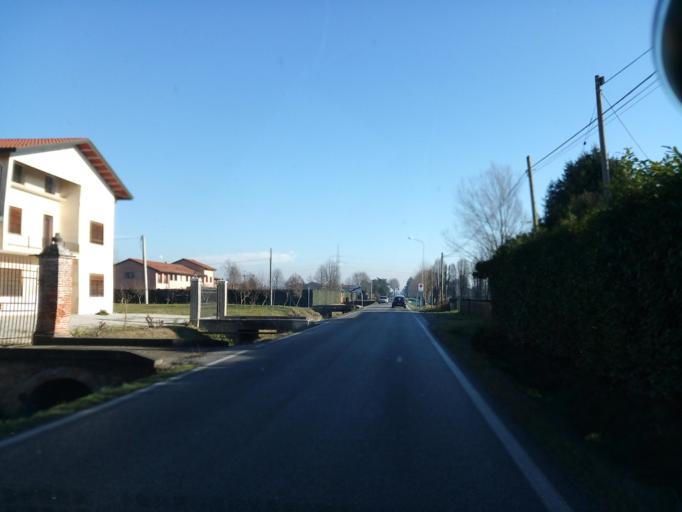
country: IT
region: Veneto
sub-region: Provincia di Venezia
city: Veternigo
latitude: 45.5124
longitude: 12.0649
